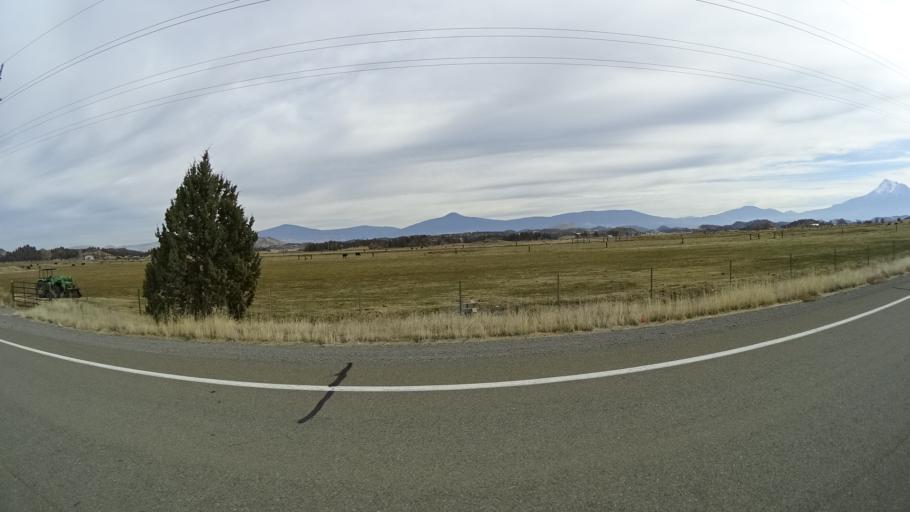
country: US
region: California
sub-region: Siskiyou County
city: Montague
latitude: 41.6654
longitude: -122.5222
